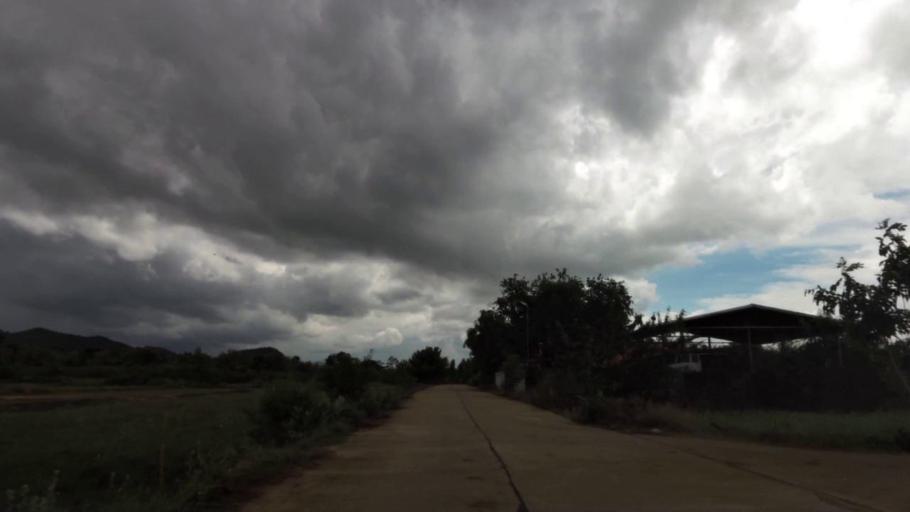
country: TH
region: Nakhon Sawan
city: Phai Sali
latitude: 15.6031
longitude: 100.6773
